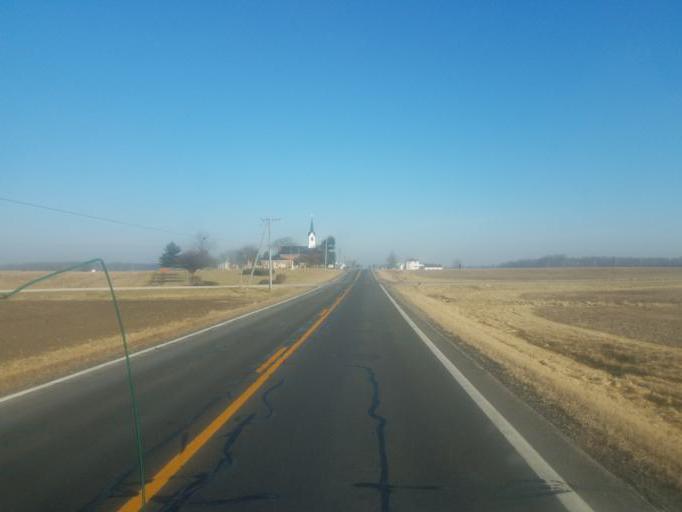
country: US
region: Ohio
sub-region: Crawford County
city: Bucyrus
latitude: 40.9787
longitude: -82.9301
